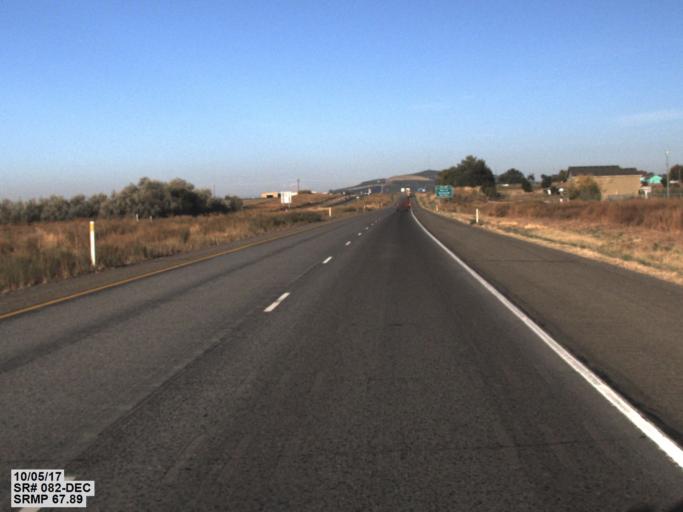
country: US
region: Washington
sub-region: Yakima County
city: Sunnyside
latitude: 46.3061
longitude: -120.0004
